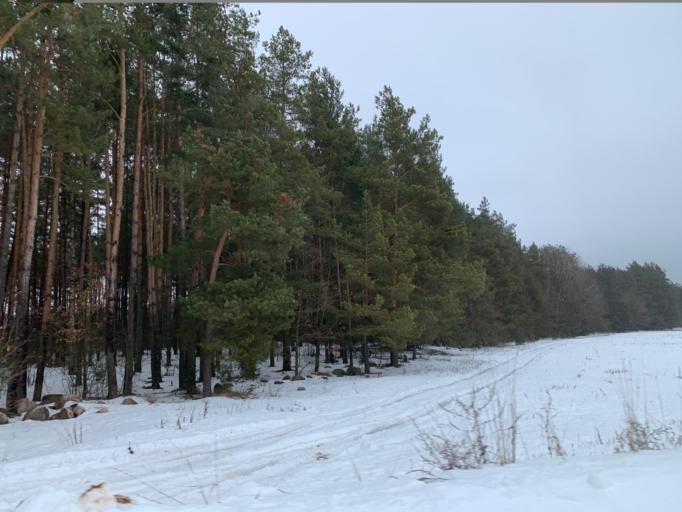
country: BY
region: Minsk
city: Il'ya
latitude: 54.5531
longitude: 27.2843
